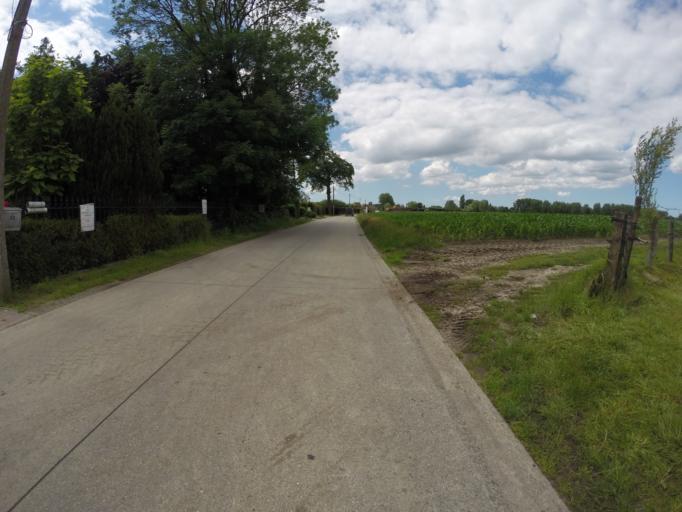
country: BE
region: Flanders
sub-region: Provincie Oost-Vlaanderen
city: Aalter
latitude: 51.1047
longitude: 3.5049
